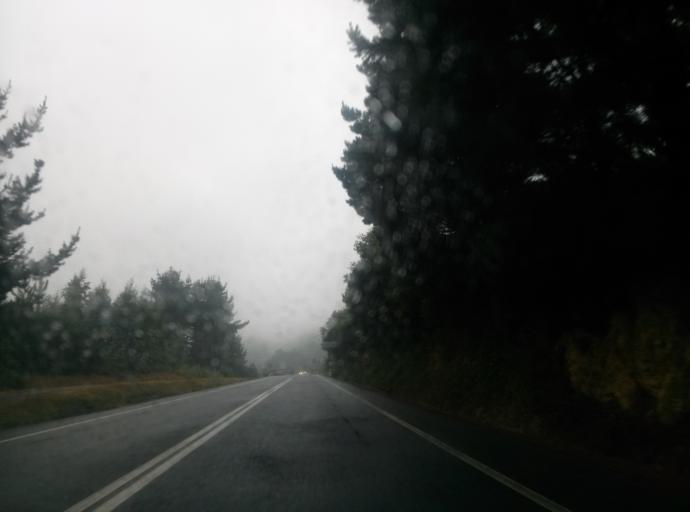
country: ES
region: Galicia
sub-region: Provincia de Lugo
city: Muras
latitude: 43.5468
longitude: -7.6517
